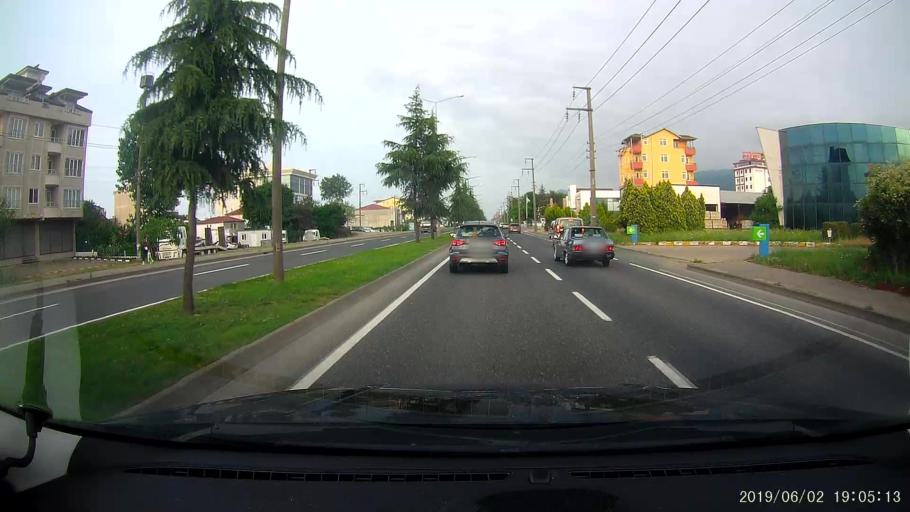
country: TR
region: Ordu
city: Ordu
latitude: 40.9773
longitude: 37.9502
